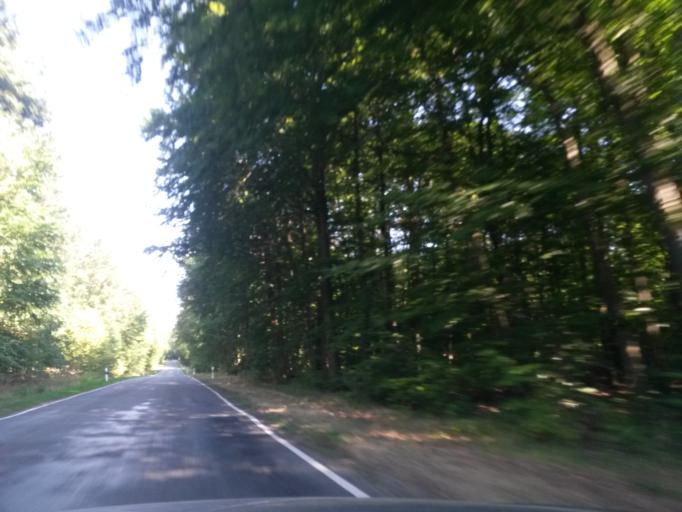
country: DE
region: Brandenburg
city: Wiesenburg
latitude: 52.0339
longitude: 12.3753
